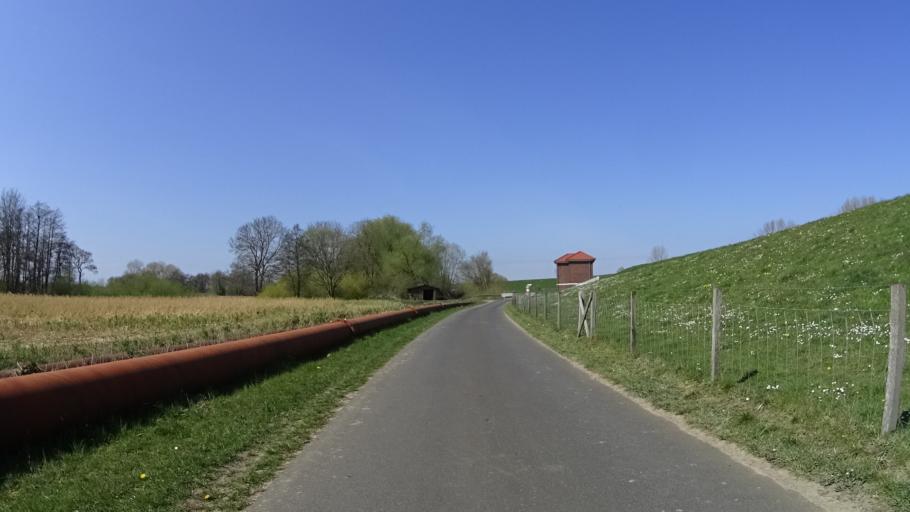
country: DE
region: Lower Saxony
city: Weener
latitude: 53.1025
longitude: 7.3273
